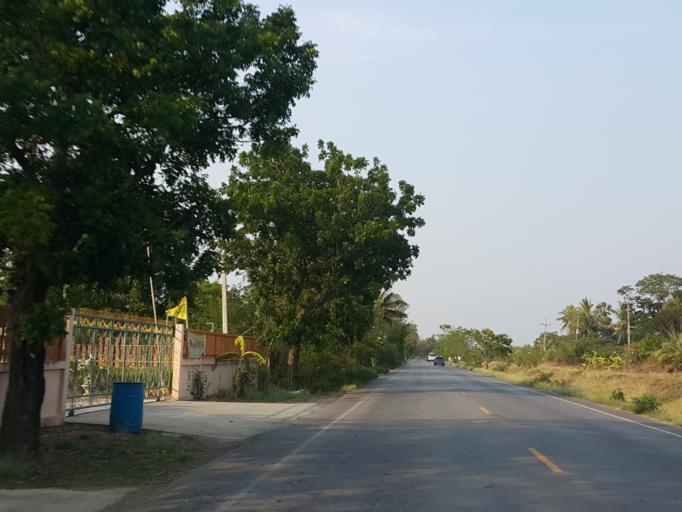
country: TH
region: Chai Nat
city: Sankhaburi
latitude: 15.0159
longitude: 100.1354
